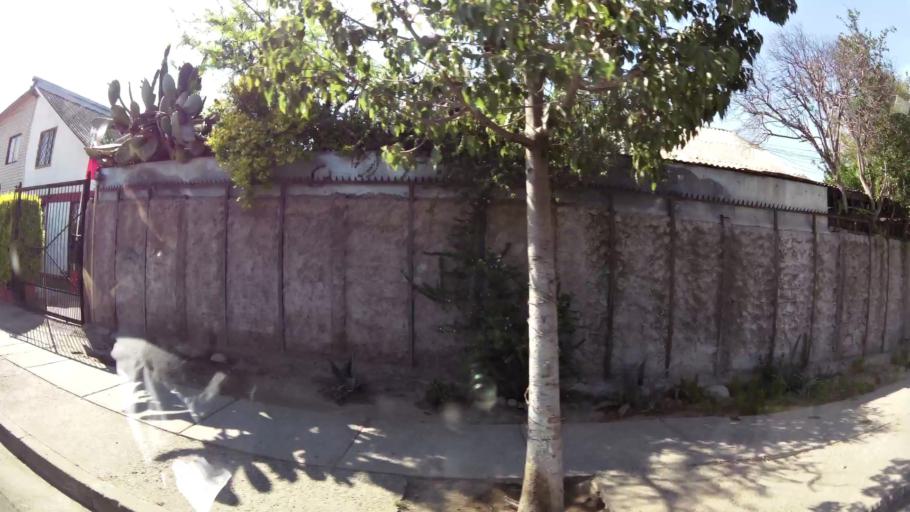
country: CL
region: Santiago Metropolitan
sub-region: Provincia de Maipo
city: San Bernardo
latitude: -33.5910
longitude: -70.6877
